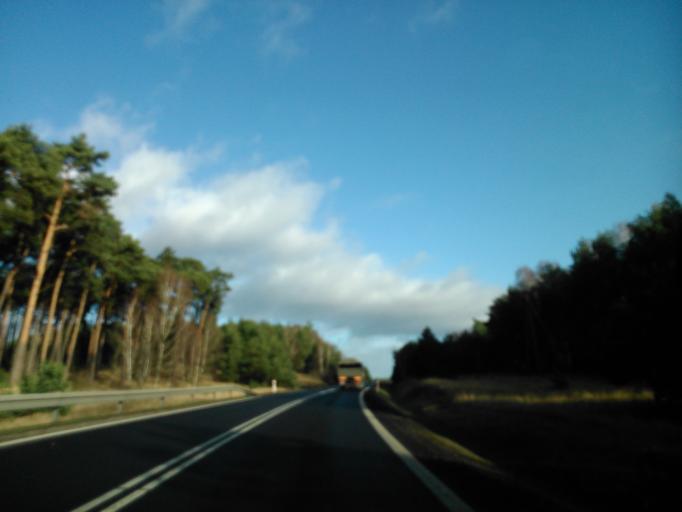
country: PL
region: Kujawsko-Pomorskie
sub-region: Powiat torunski
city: Wielka Nieszawka
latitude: 52.9427
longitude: 18.5190
